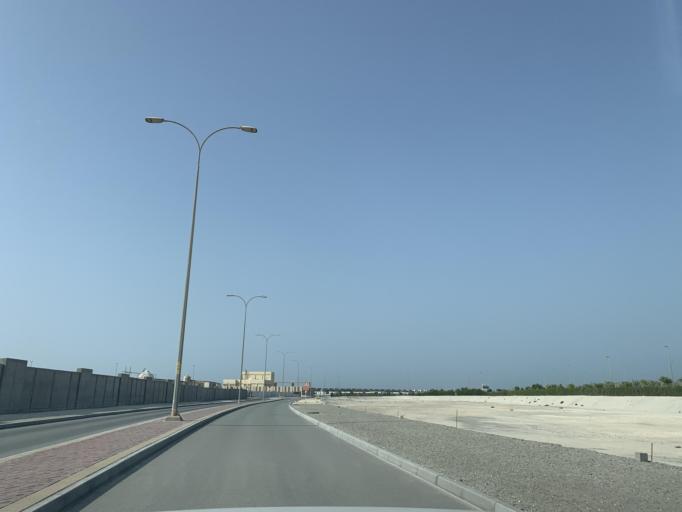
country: BH
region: Muharraq
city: Al Muharraq
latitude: 26.3094
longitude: 50.6389
